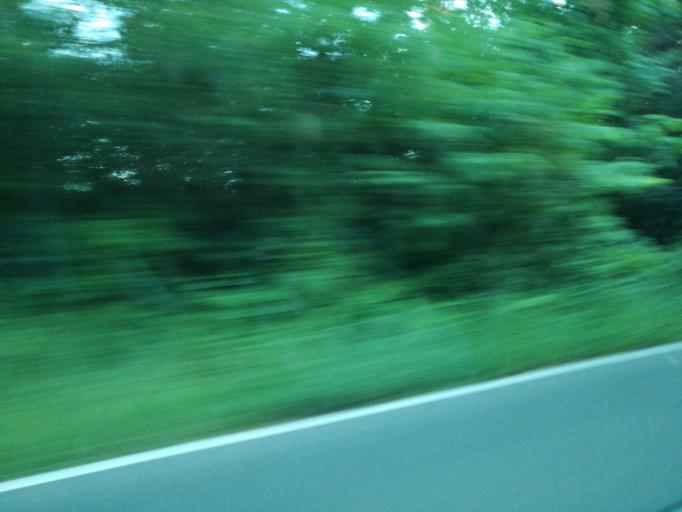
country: RO
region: Constanta
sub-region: Comuna Douazeci si Trei August
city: Douazeci si Trei August
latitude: 43.8589
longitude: 28.5864
